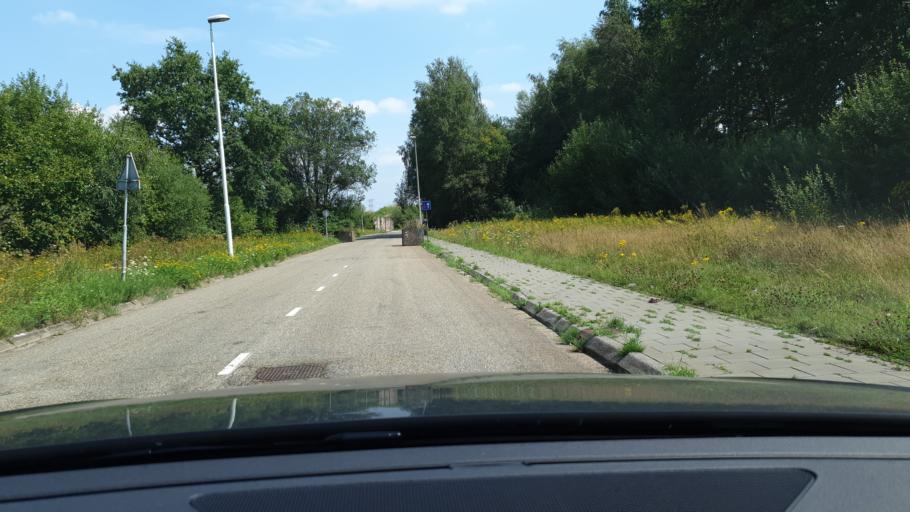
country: NL
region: North Brabant
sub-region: Gemeente Son en Breugel
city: Son
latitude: 51.4926
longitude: 5.4578
